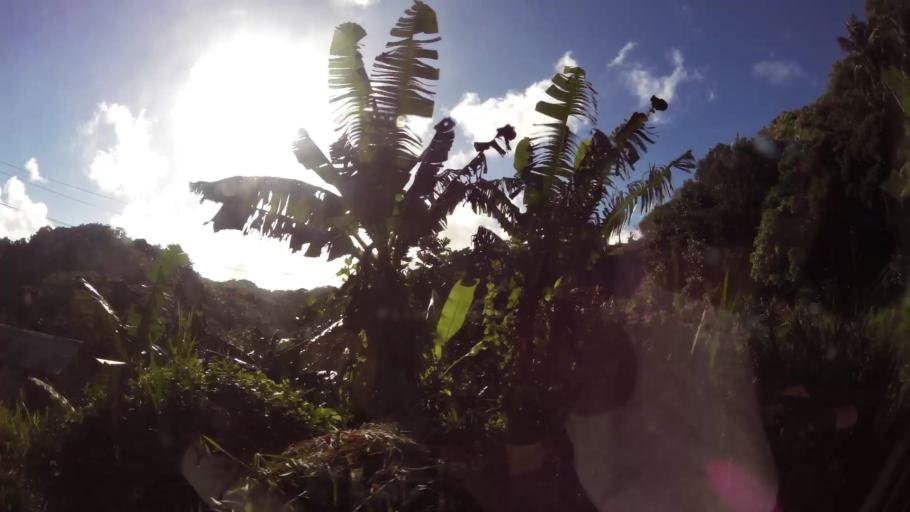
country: DM
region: Saint John
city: Portsmouth
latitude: 15.5812
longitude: -61.4170
